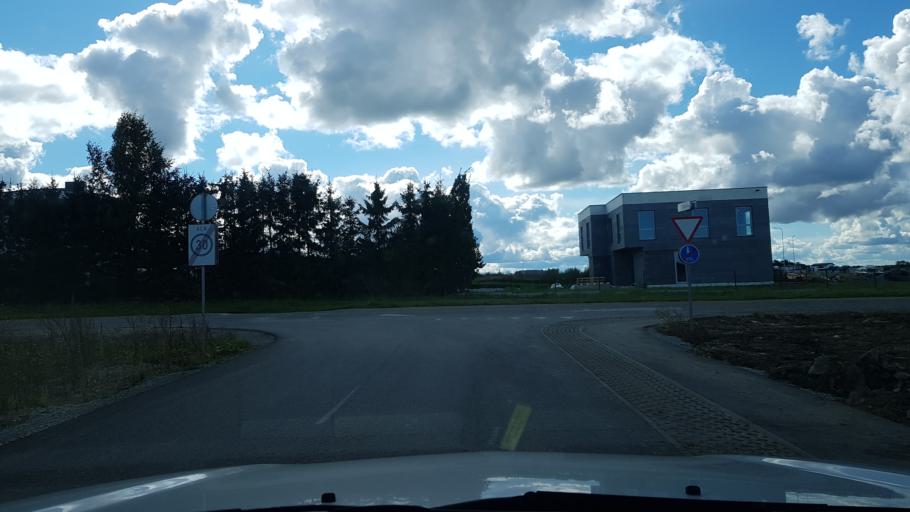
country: EE
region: Harju
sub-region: Tallinna linn
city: Tallinn
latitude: 59.3829
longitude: 24.8093
